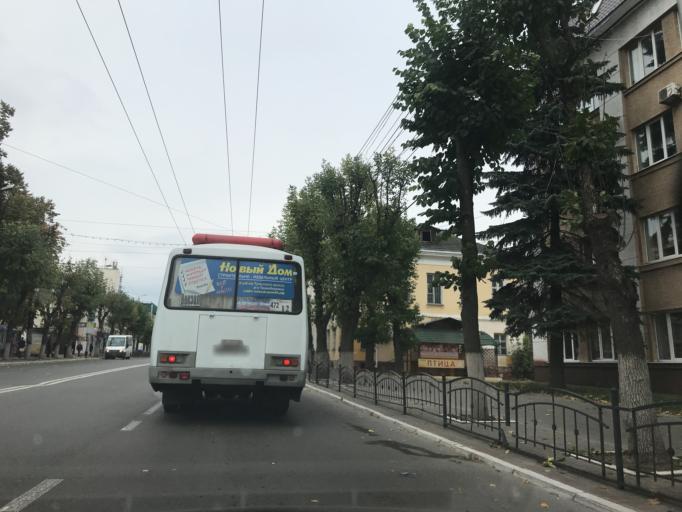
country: RU
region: Kaluga
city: Kaluga
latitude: 54.5123
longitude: 36.2630
